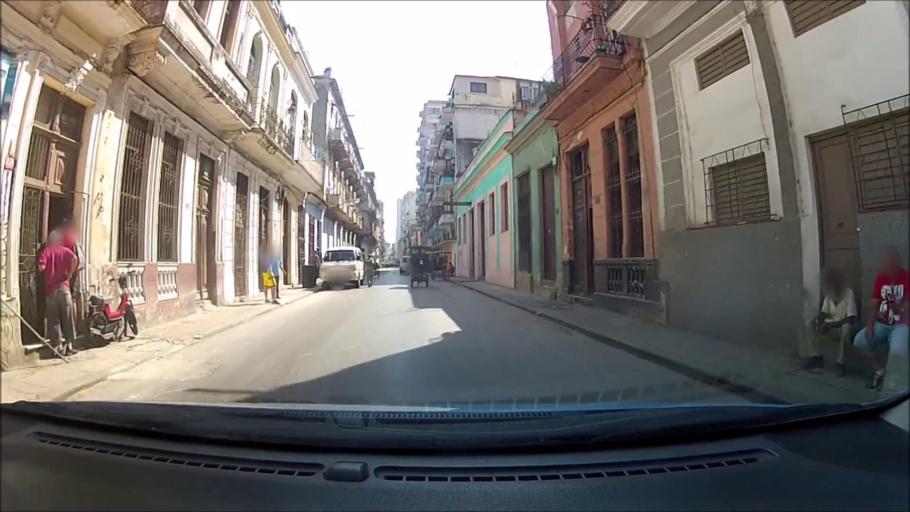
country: CU
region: La Habana
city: Centro Habana
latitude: 23.1399
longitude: -82.3685
